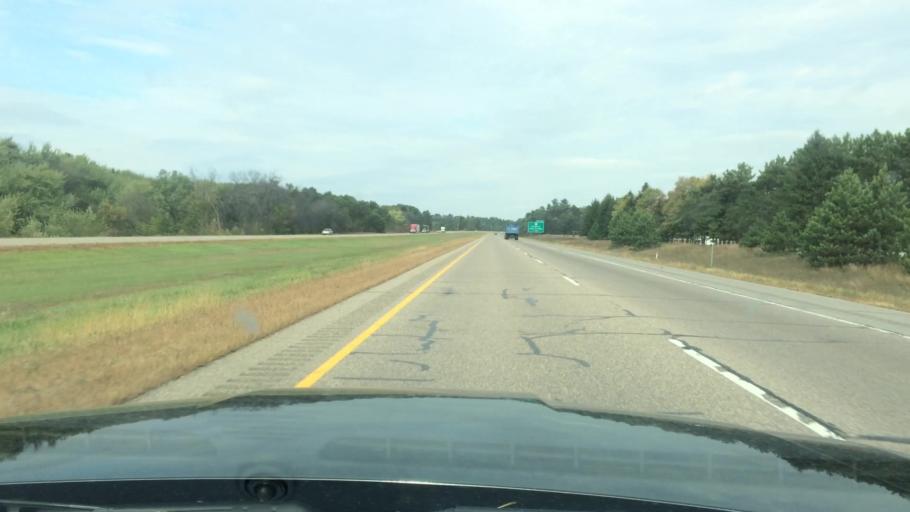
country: US
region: Wisconsin
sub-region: Portage County
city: Stevens Point
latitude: 44.6534
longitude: -89.6397
